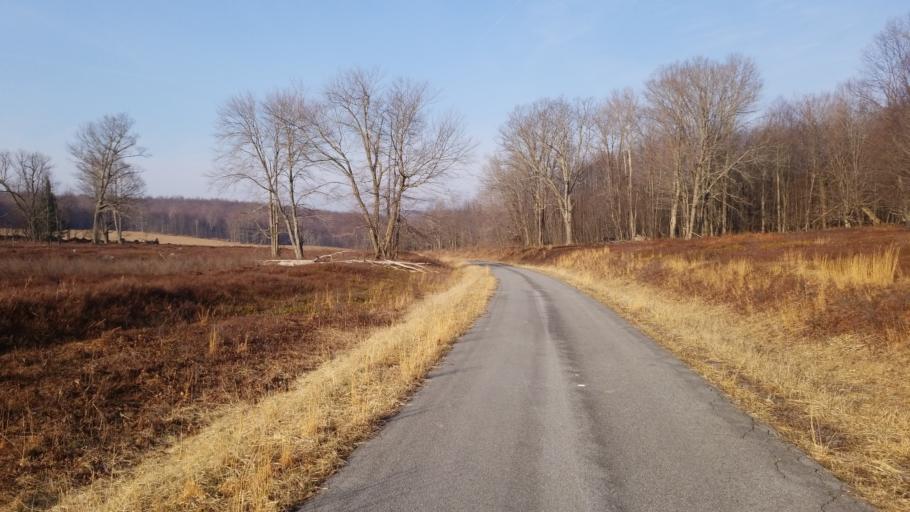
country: US
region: Pennsylvania
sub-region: Clearfield County
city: Shiloh
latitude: 41.2237
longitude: -78.2332
